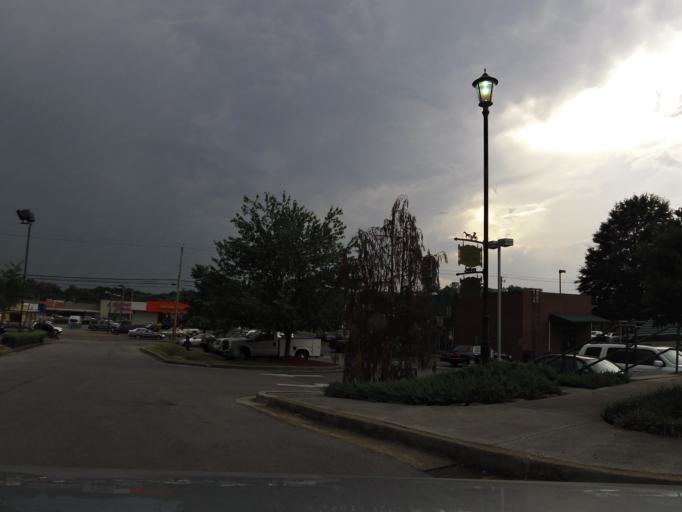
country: US
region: Tennessee
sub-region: Knox County
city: Knoxville
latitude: 36.0270
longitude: -83.9267
